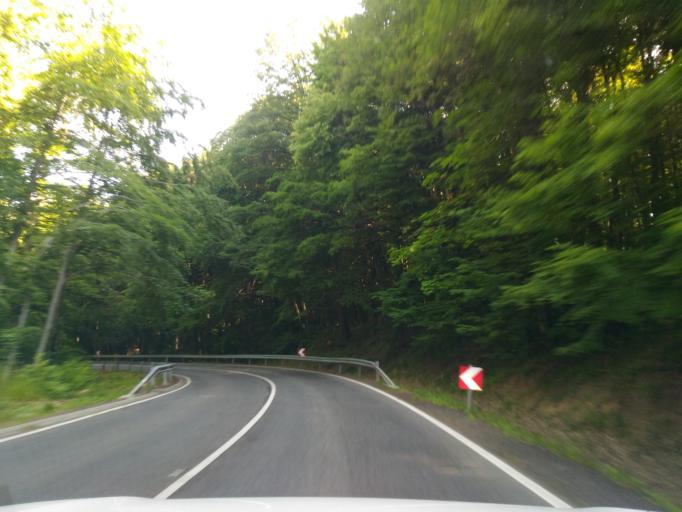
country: HU
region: Baranya
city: Komlo
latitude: 46.1790
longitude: 18.2650
